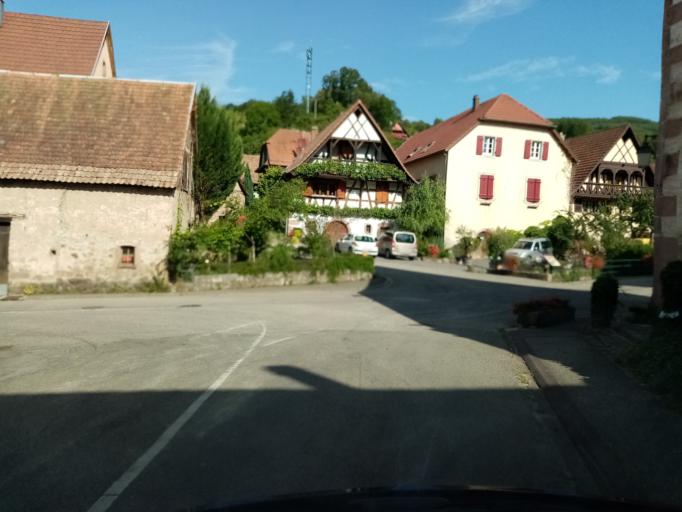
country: FR
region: Alsace
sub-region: Departement du Bas-Rhin
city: Ville
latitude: 48.3566
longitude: 7.3188
